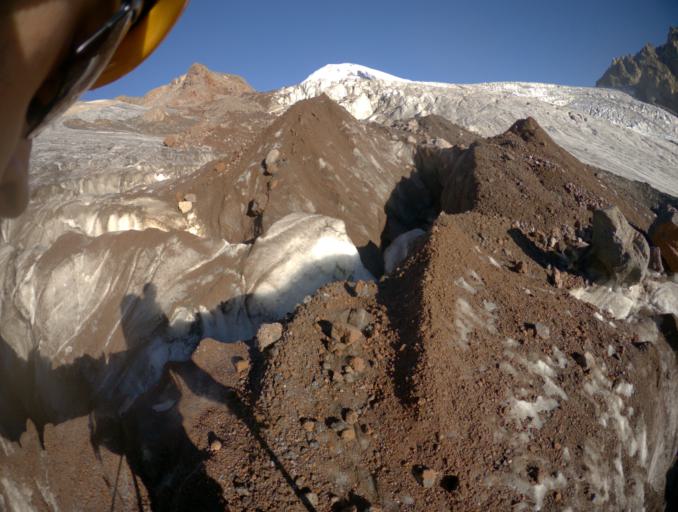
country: RU
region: Kabardino-Balkariya
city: Terskol
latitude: 43.3182
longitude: 42.5184
